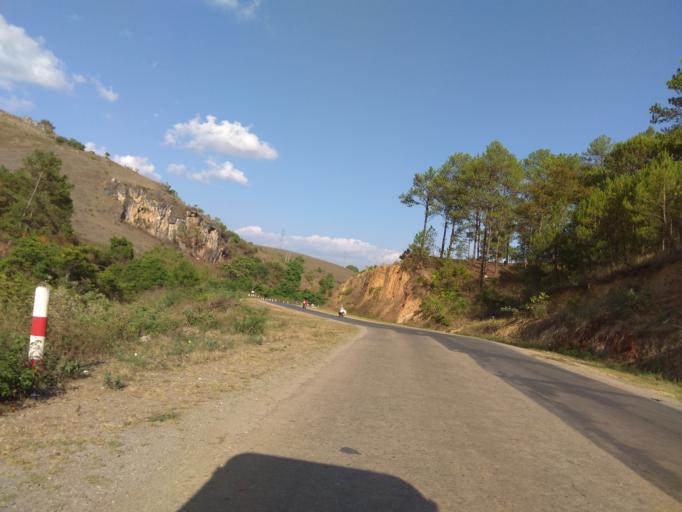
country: MM
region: Shan
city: Taunggyi
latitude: 20.6495
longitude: 96.5974
